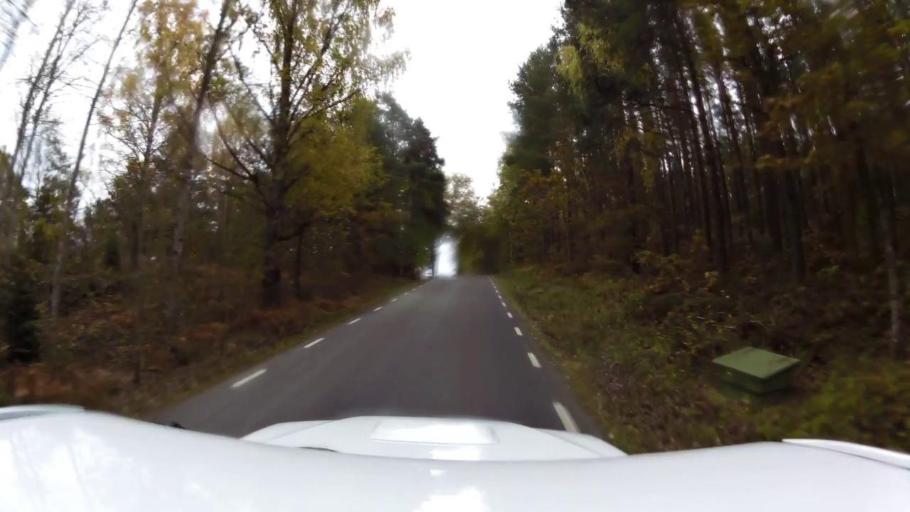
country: SE
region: OEstergoetland
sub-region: Linkopings Kommun
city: Linghem
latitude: 58.3558
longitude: 15.8521
